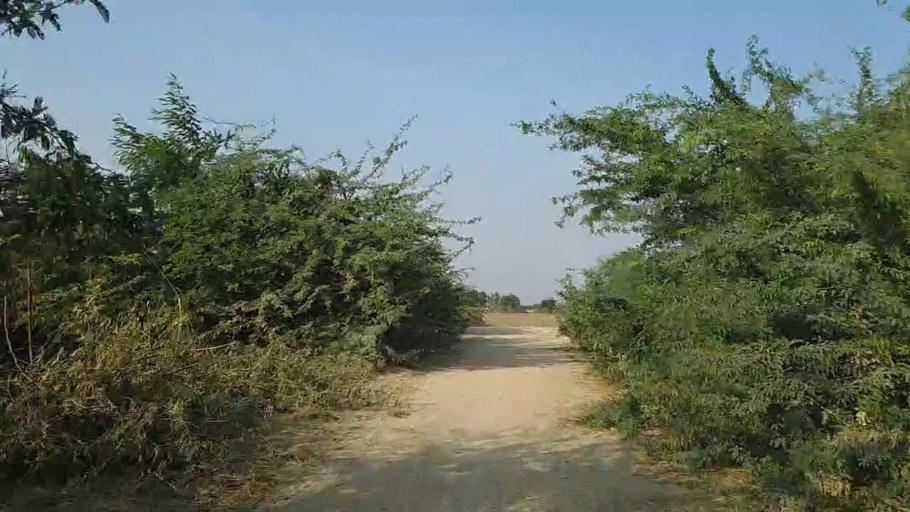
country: PK
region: Sindh
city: Mirpur Sakro
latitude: 24.5994
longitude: 67.6493
